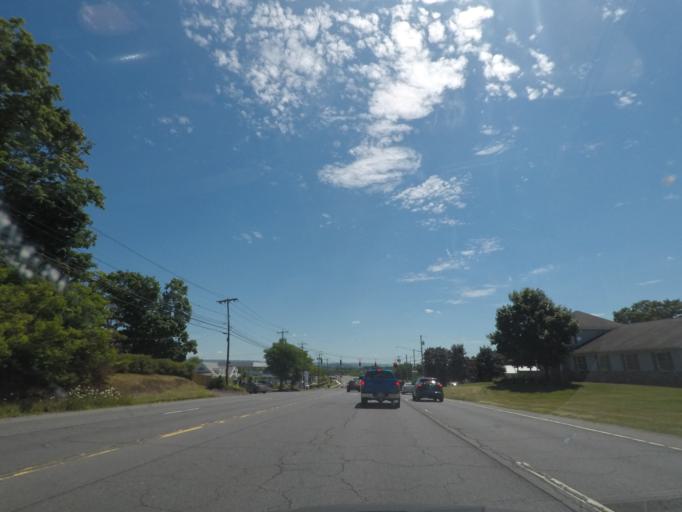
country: US
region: New York
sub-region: Albany County
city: Watervliet
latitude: 42.7405
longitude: -73.7375
